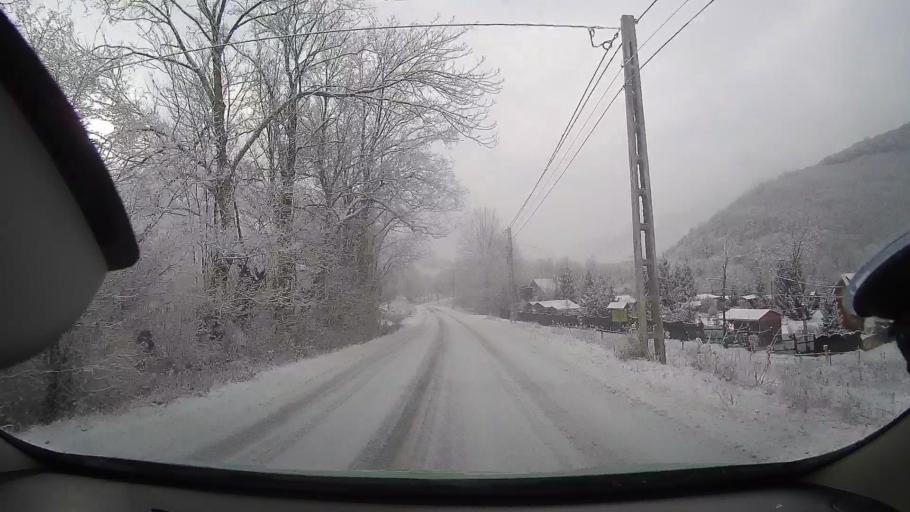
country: RO
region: Alba
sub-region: Comuna Rimetea
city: Rimetea
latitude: 46.4717
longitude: 23.5837
